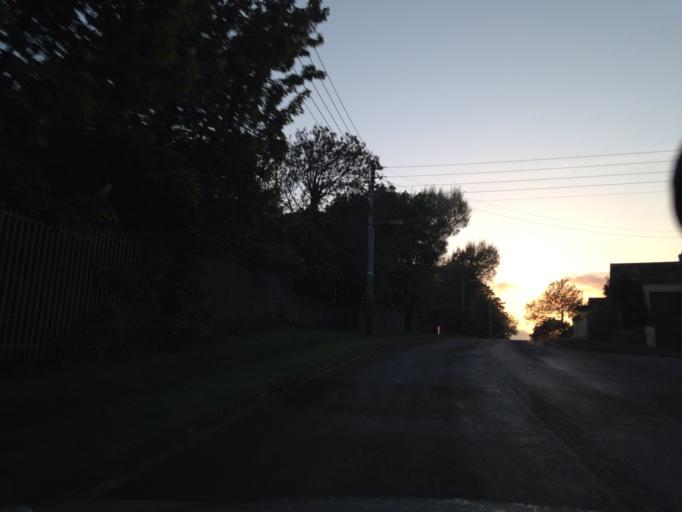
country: IE
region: Connaught
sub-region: County Galway
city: Gaillimh
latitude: 53.2726
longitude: -9.0264
